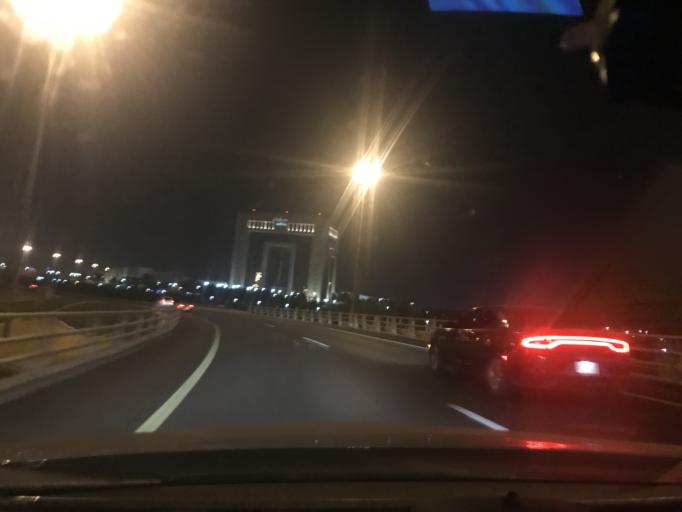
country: SA
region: Ar Riyad
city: Riyadh
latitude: 24.7936
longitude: 46.7238
